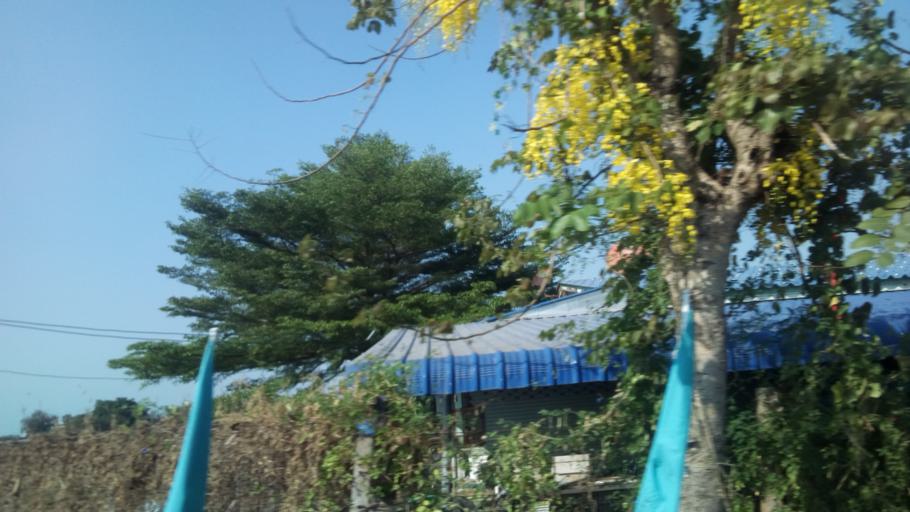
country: TH
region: Nonthaburi
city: Bang Bua Thong
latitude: 13.9357
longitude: 100.3694
